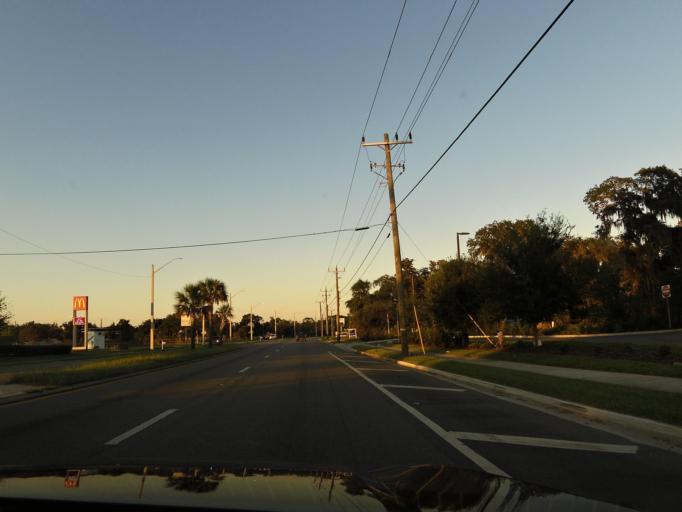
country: US
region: Florida
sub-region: Putnam County
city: East Palatka
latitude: 29.6445
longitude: -81.6048
